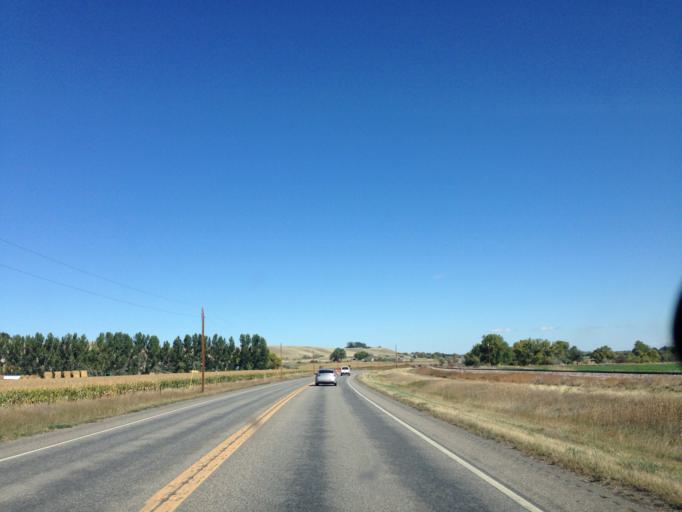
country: US
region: Montana
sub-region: Yellowstone County
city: Laurel
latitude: 45.5715
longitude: -108.8360
